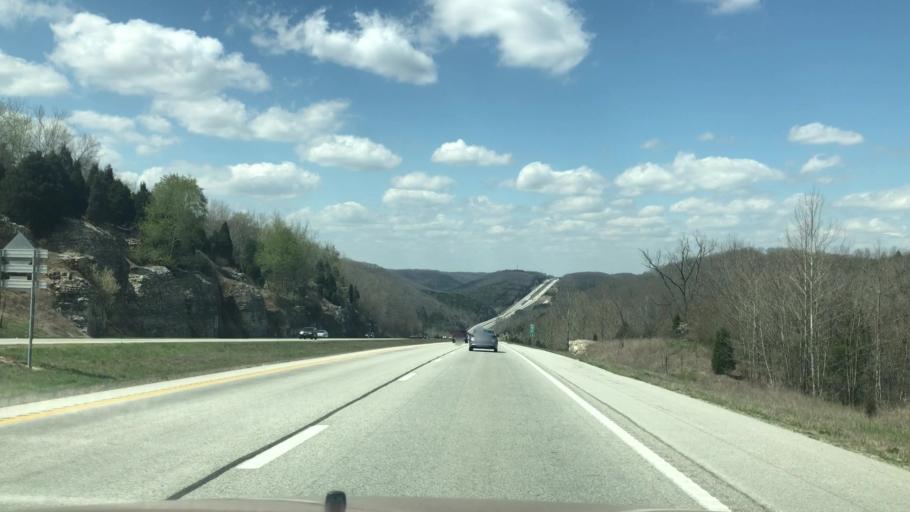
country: US
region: Missouri
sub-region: Taney County
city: Merriam Woods
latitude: 36.8479
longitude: -93.2210
